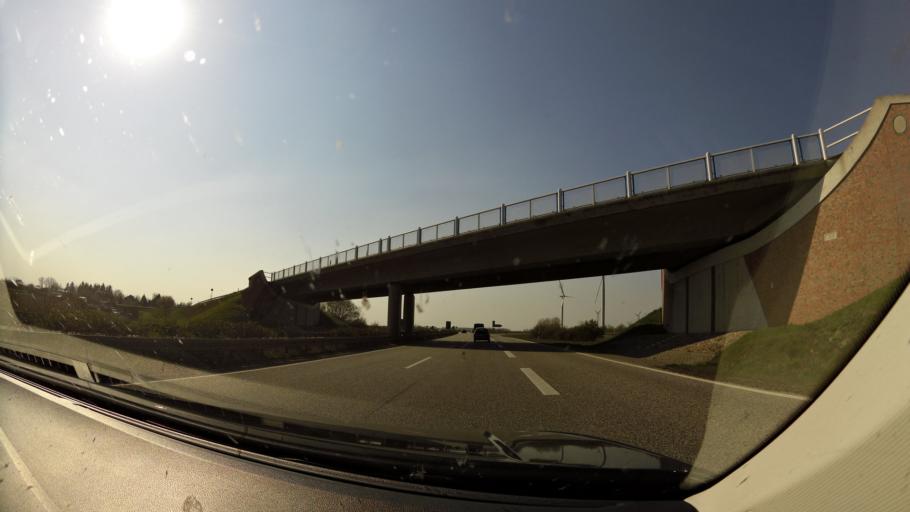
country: DE
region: Mecklenburg-Vorpommern
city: Grimmen
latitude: 54.0883
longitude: 12.9819
